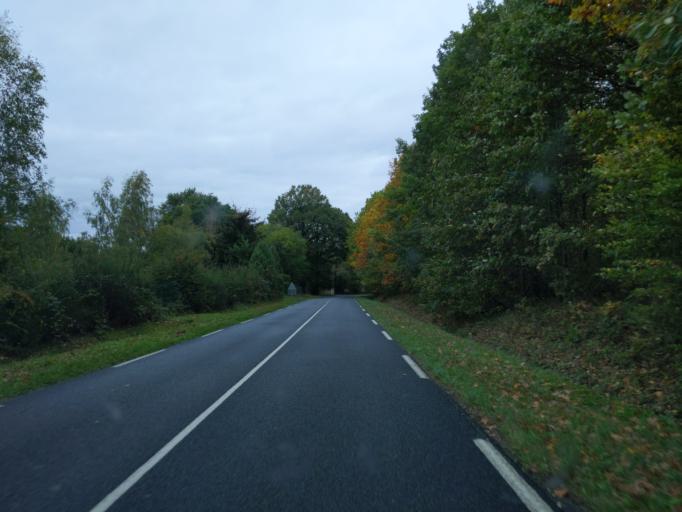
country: FR
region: Ile-de-France
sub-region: Departement des Yvelines
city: Bullion
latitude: 48.6303
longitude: 1.9976
